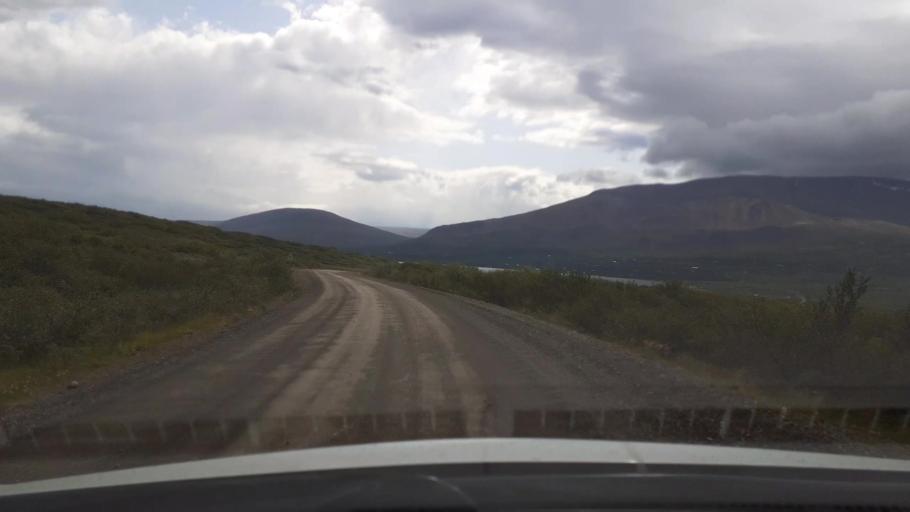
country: IS
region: West
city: Borgarnes
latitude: 64.5524
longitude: -21.6235
